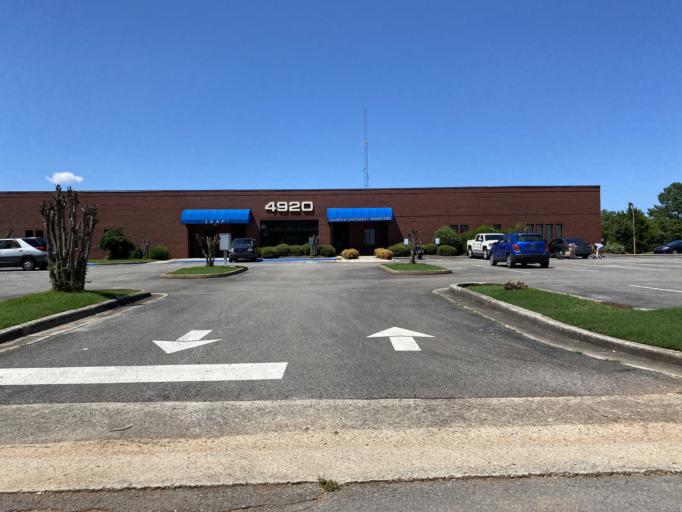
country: US
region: Alabama
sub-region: Madison County
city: Redstone Arsenal
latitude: 34.7434
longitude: -86.6594
